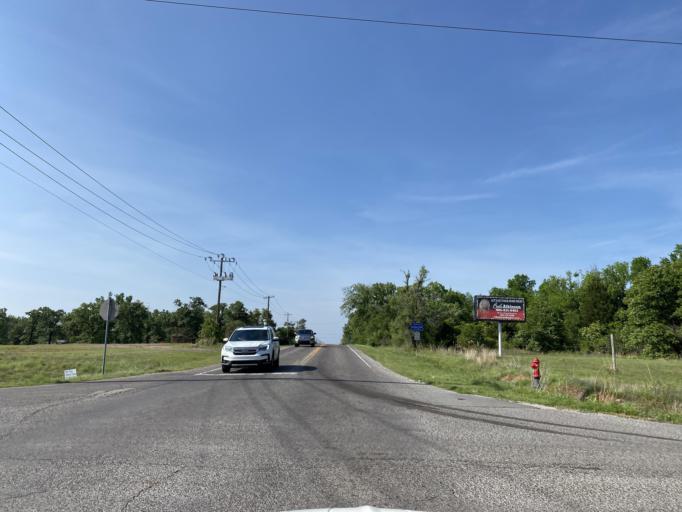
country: US
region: Oklahoma
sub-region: Oklahoma County
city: Nicoma Park
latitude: 35.4785
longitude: -97.3356
